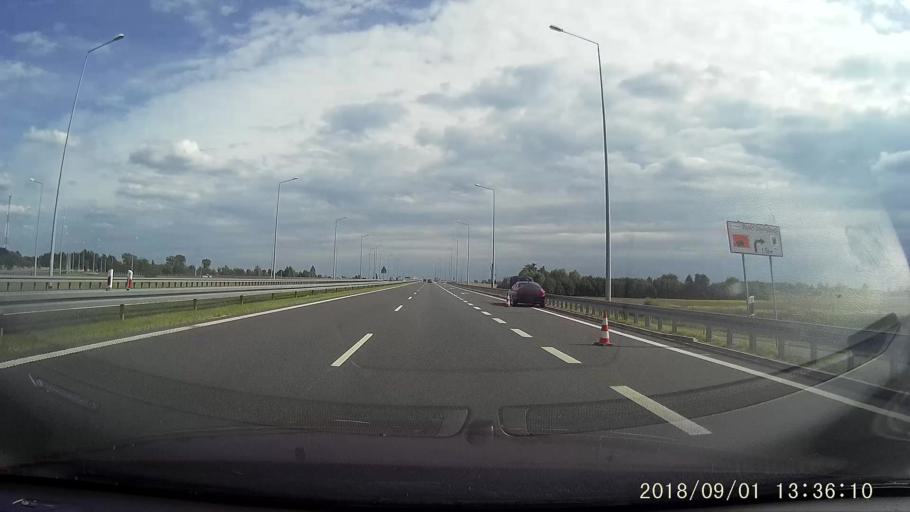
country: PL
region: West Pomeranian Voivodeship
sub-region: Powiat pyrzycki
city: Lipiany
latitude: 52.9532
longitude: 14.9455
